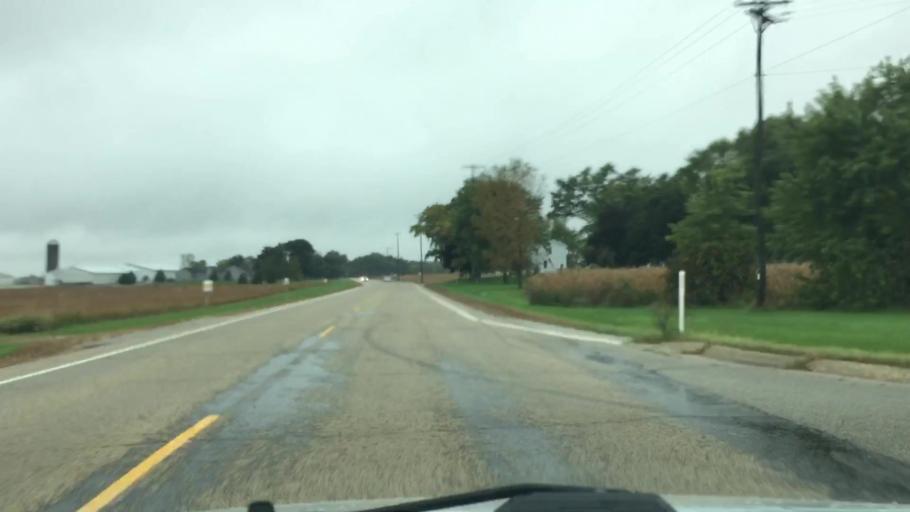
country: US
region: Wisconsin
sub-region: Jefferson County
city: Palmyra
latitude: 42.8787
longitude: -88.6304
